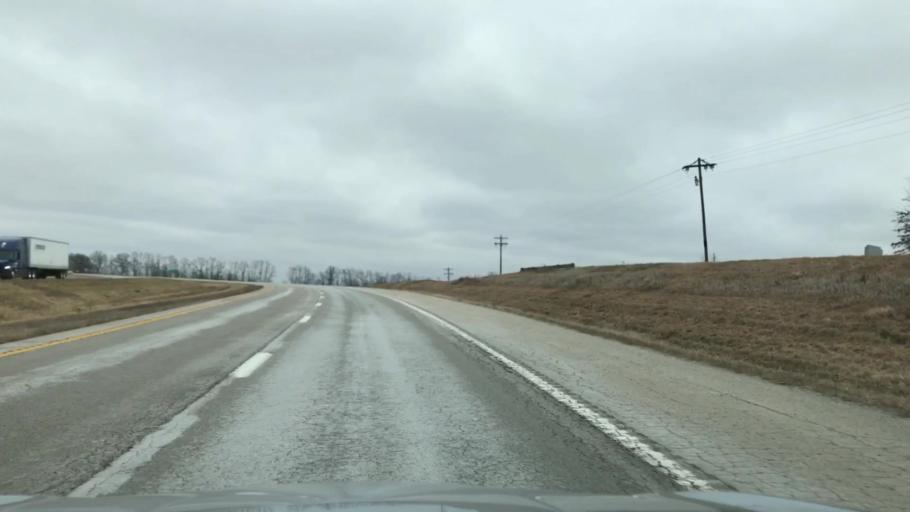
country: US
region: Missouri
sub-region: Livingston County
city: Chillicothe
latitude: 39.7374
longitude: -93.6348
